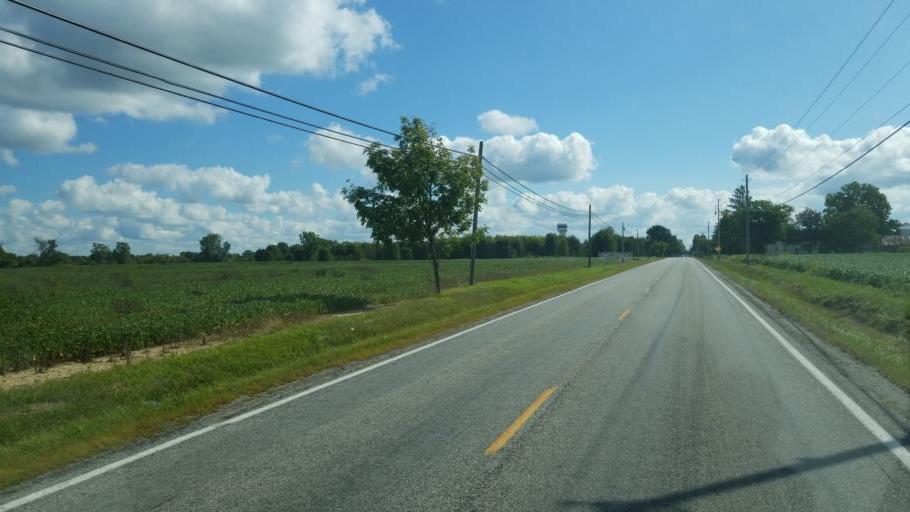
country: US
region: Ohio
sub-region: Lorain County
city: Lagrange
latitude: 41.2372
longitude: -82.1334
